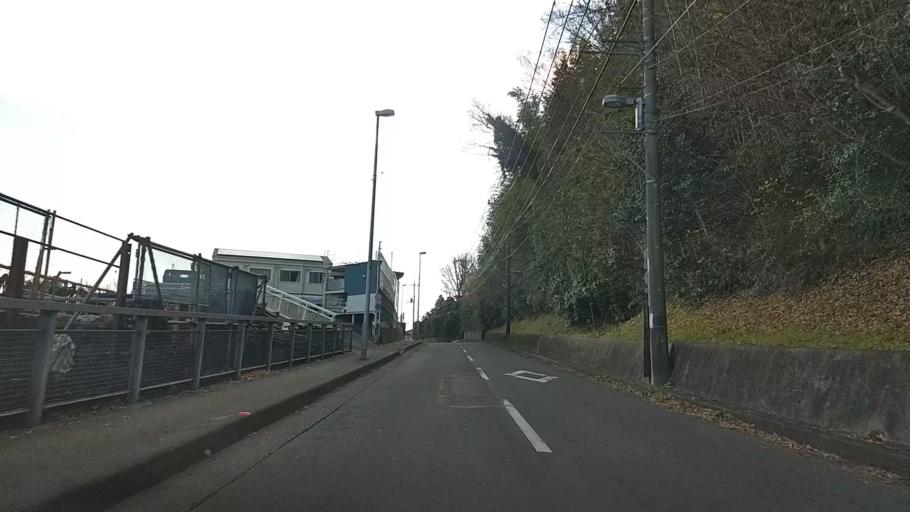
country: JP
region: Kanagawa
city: Atsugi
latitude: 35.4284
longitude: 139.3266
